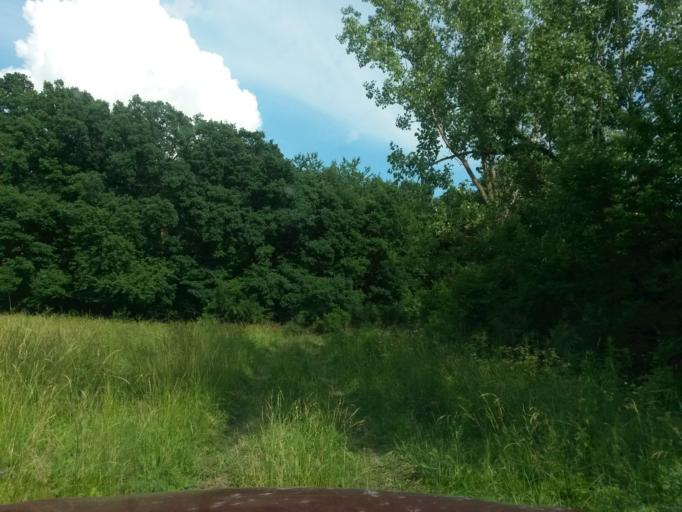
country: SK
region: Kosicky
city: Moldava nad Bodvou
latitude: 48.6195
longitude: 21.1046
